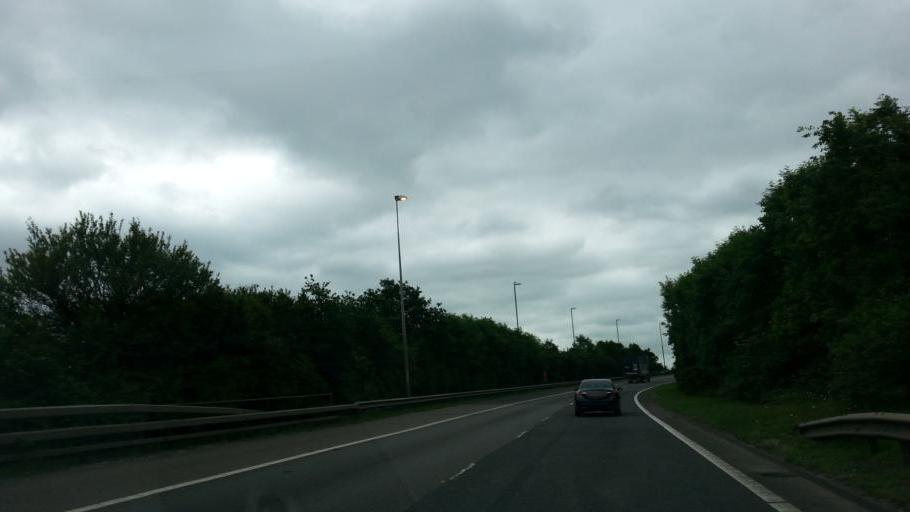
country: GB
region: England
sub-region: Warwickshire
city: Water Orton
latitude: 52.5125
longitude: -1.7251
